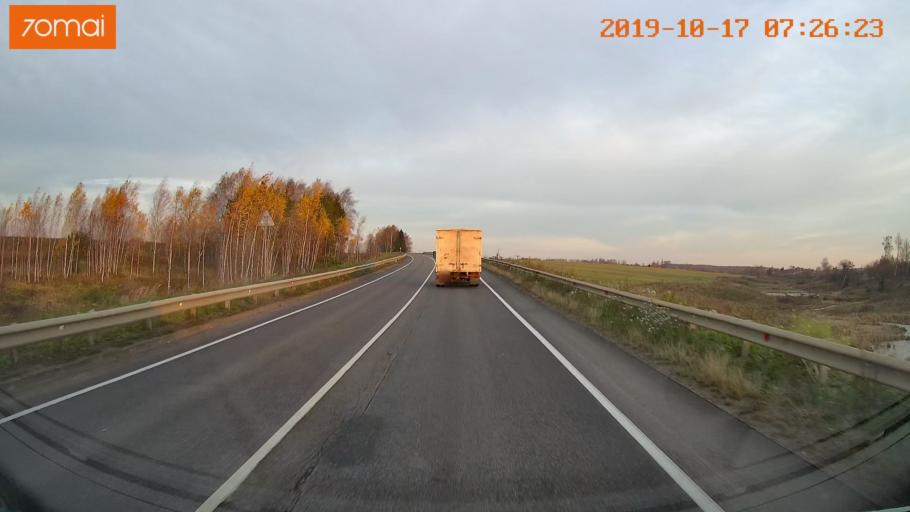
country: RU
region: Ivanovo
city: Gavrilov Posad
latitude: 56.3569
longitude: 40.0929
